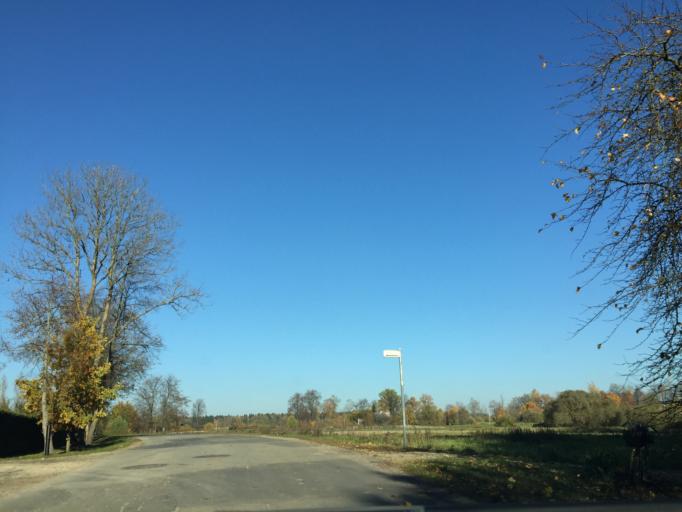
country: LT
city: Salantai
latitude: 56.0010
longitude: 21.6783
